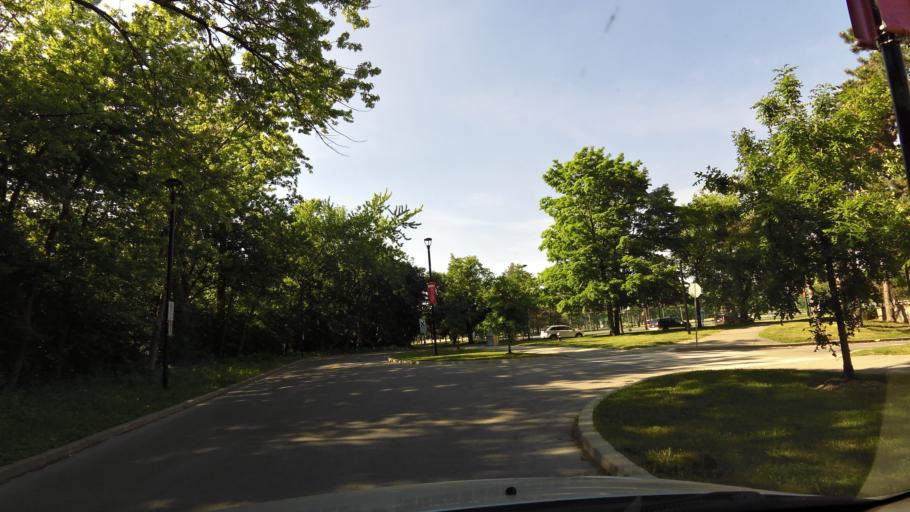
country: CA
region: Ontario
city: Concord
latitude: 43.7761
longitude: -79.5045
